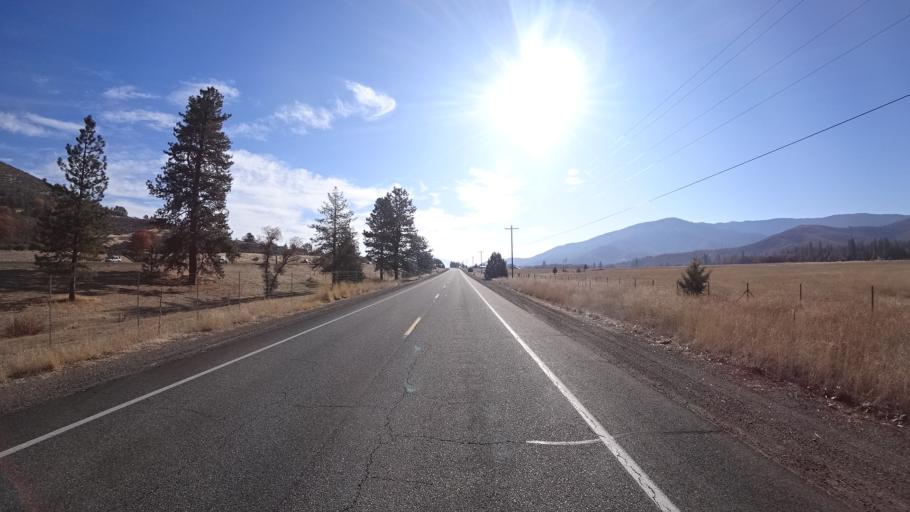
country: US
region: California
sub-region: Siskiyou County
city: Yreka
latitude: 41.6805
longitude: -122.6310
